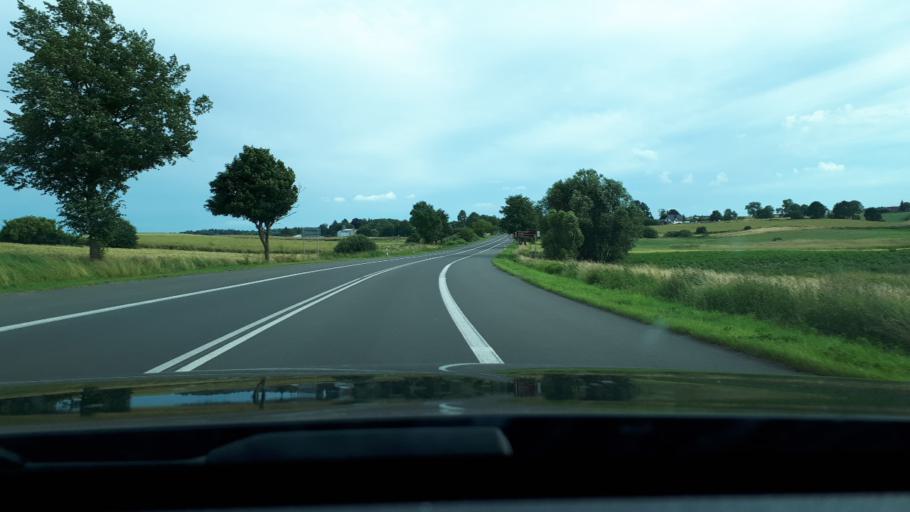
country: PL
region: Warmian-Masurian Voivodeship
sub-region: Powiat ostrodzki
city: Ostroda
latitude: 53.6546
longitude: 20.0516
